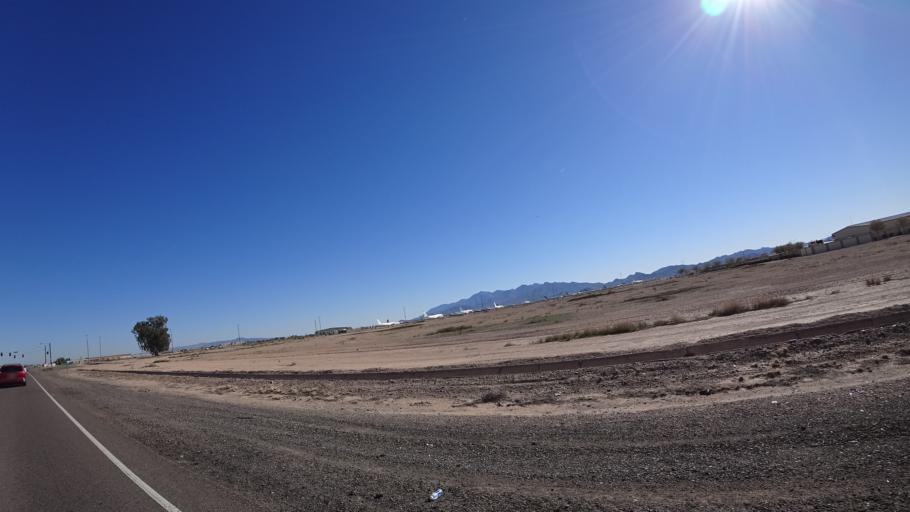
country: US
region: Arizona
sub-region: Maricopa County
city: Goodyear
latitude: 33.4355
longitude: -112.3779
